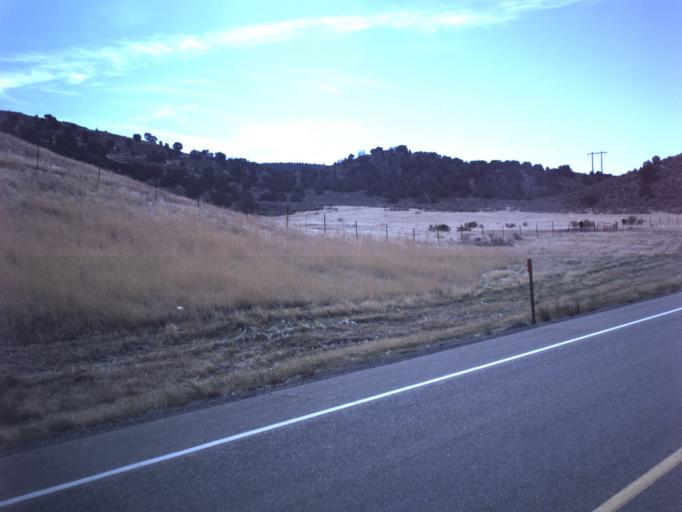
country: US
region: Utah
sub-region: Sanpete County
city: Gunnison
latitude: 39.3741
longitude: -111.9285
